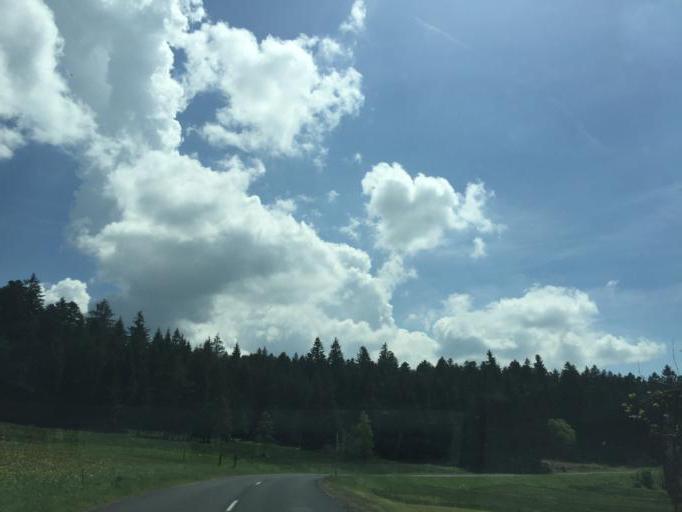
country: FR
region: Rhone-Alpes
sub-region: Departement de la Loire
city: Saint-Sauveur-en-Rue
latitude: 45.2961
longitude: 4.4560
